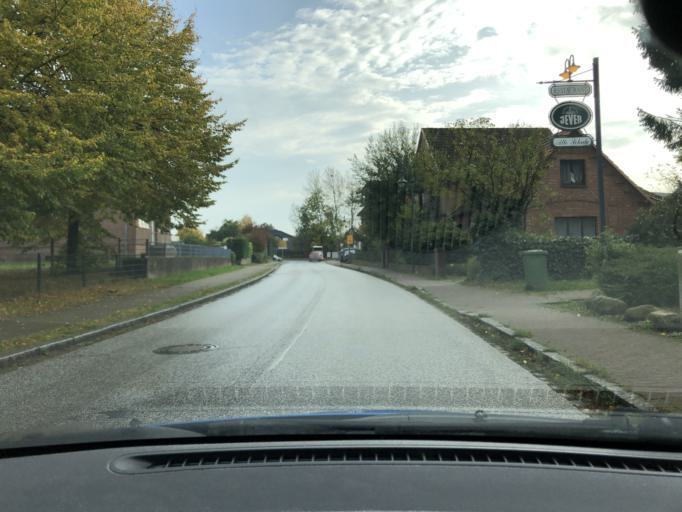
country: DE
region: Schleswig-Holstein
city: Siek
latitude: 53.6322
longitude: 10.2977
